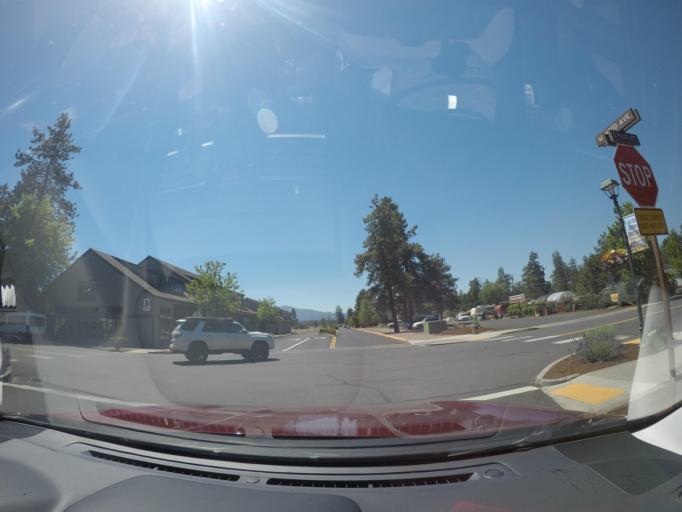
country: US
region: Oregon
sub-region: Deschutes County
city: Sisters
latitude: 44.2905
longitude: -121.5536
